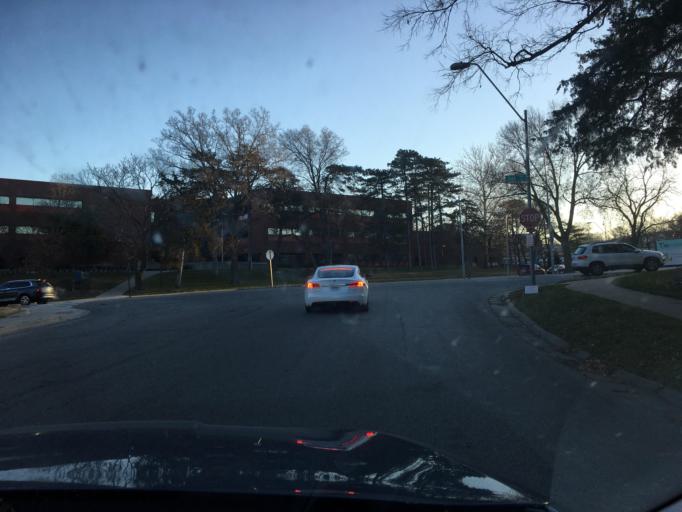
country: US
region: Kansas
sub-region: Johnson County
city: Westwood
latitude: 39.0322
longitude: -94.5832
